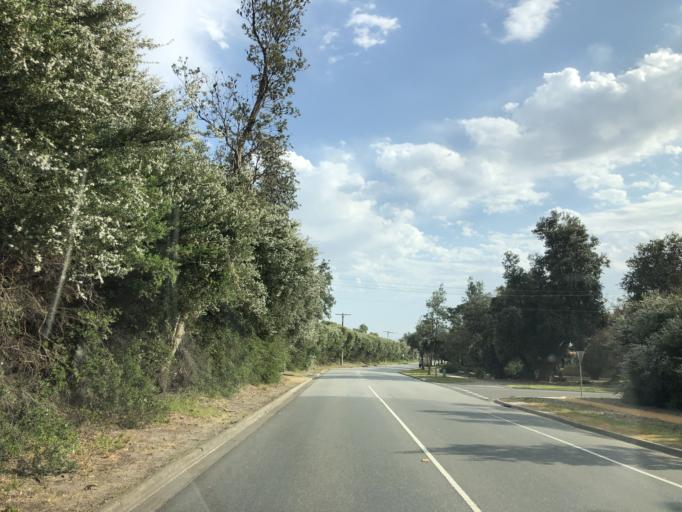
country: AU
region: Victoria
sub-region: Kingston
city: Carrum
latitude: -38.0884
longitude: 145.1277
